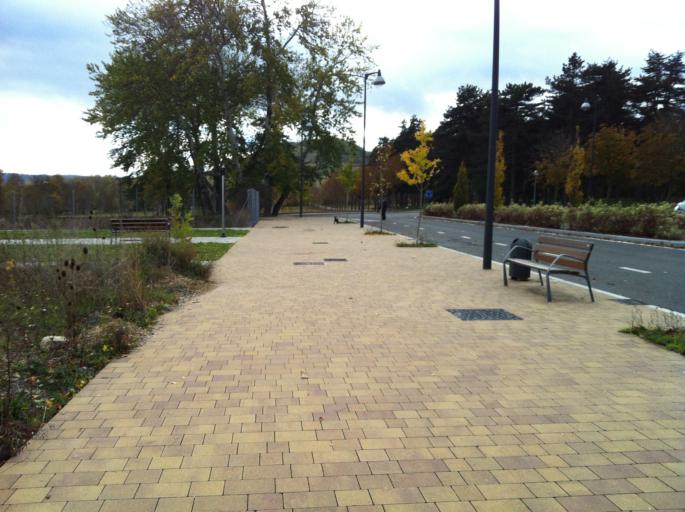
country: ES
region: Basque Country
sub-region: Provincia de Alava
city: Gasteiz / Vitoria
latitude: 42.8309
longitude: -2.6598
